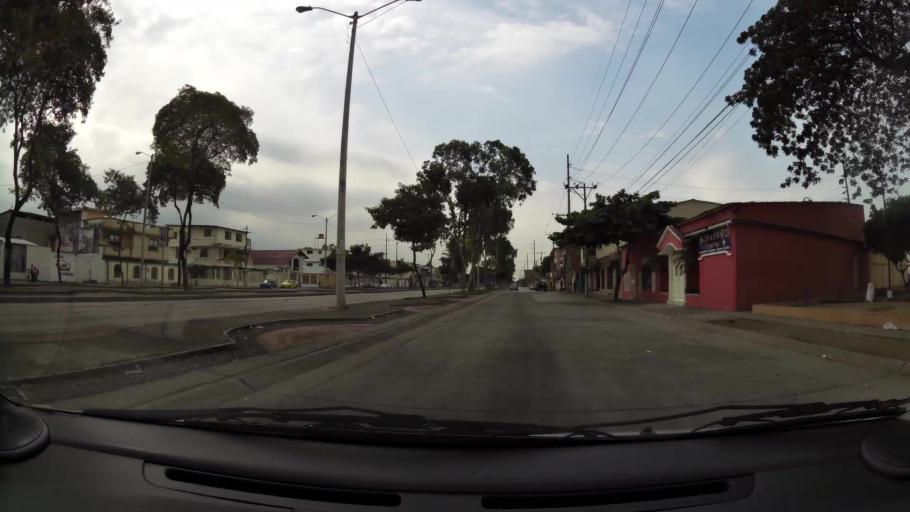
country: EC
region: Guayas
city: Eloy Alfaro
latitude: -2.1195
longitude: -79.8932
